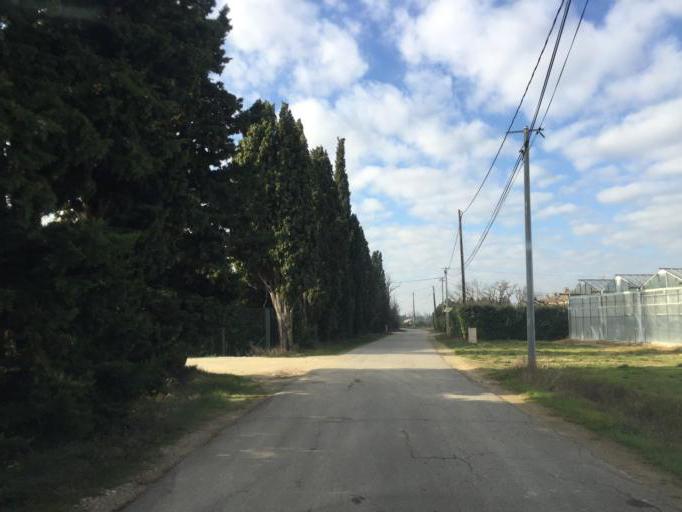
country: FR
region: Provence-Alpes-Cote d'Azur
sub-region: Departement du Vaucluse
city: Sarrians
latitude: 44.0952
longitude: 4.9369
